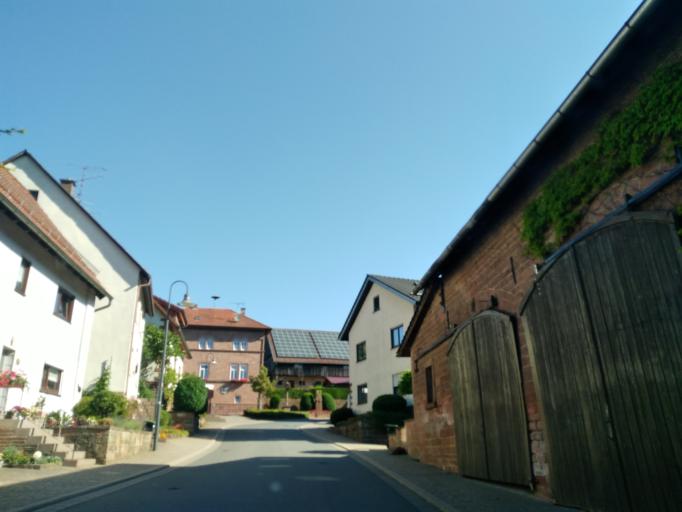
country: DE
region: Baden-Wuerttemberg
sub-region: Karlsruhe Region
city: Buchen
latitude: 49.5143
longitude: 9.2789
